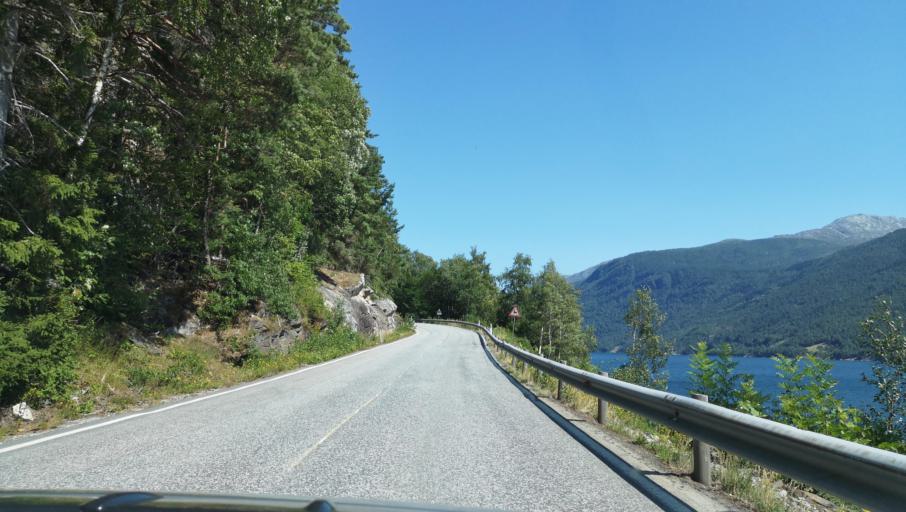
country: NO
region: Hordaland
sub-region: Ulvik
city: Ulvik
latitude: 60.4968
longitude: 6.8950
